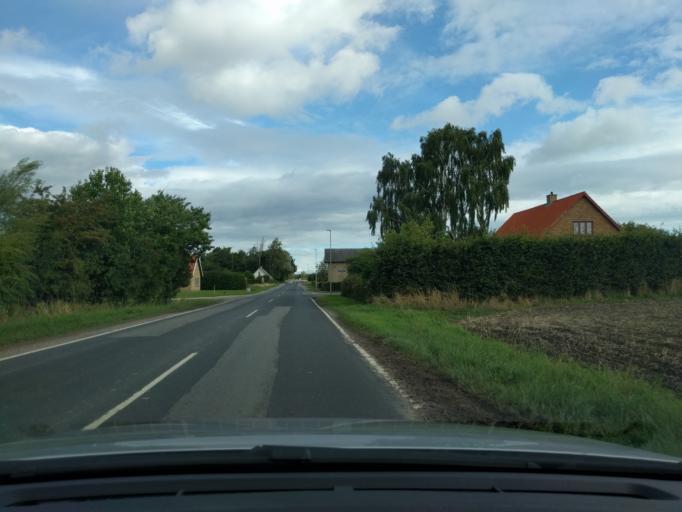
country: DK
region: South Denmark
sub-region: Nyborg Kommune
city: Ullerslev
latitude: 55.3949
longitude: 10.6657
